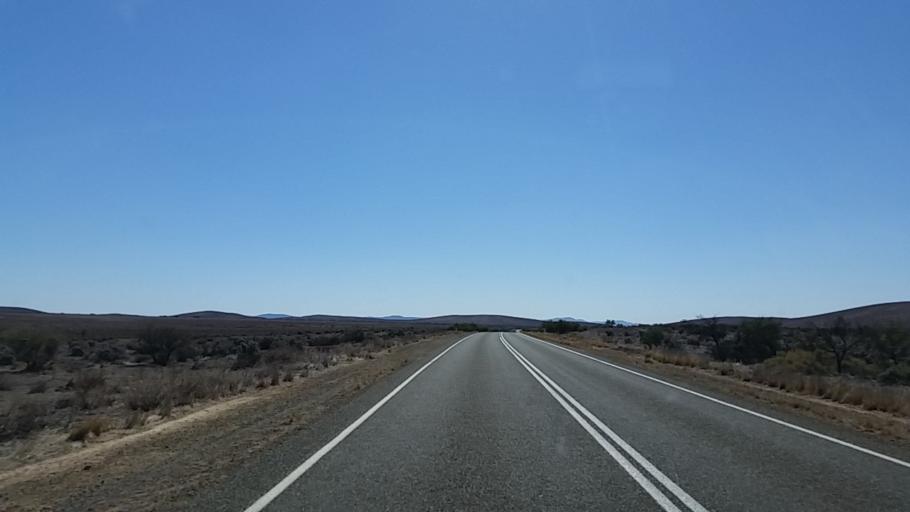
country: AU
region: South Australia
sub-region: Flinders Ranges
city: Quorn
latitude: -32.1584
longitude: 138.5295
